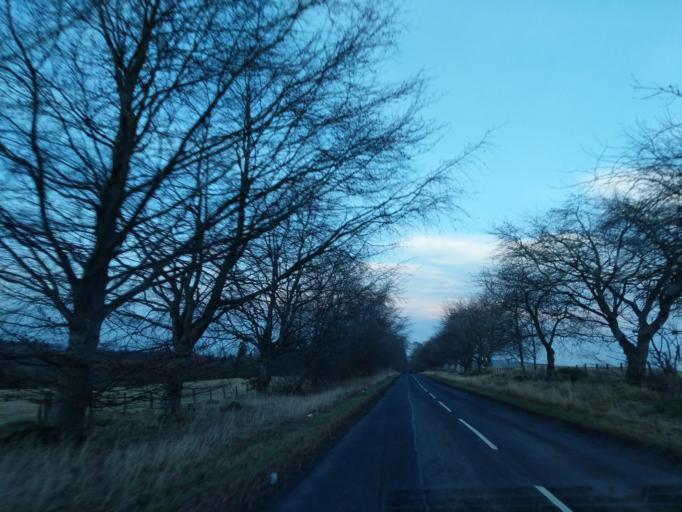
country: GB
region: Scotland
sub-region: Midlothian
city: Bonnyrigg
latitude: 55.8088
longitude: -3.1094
